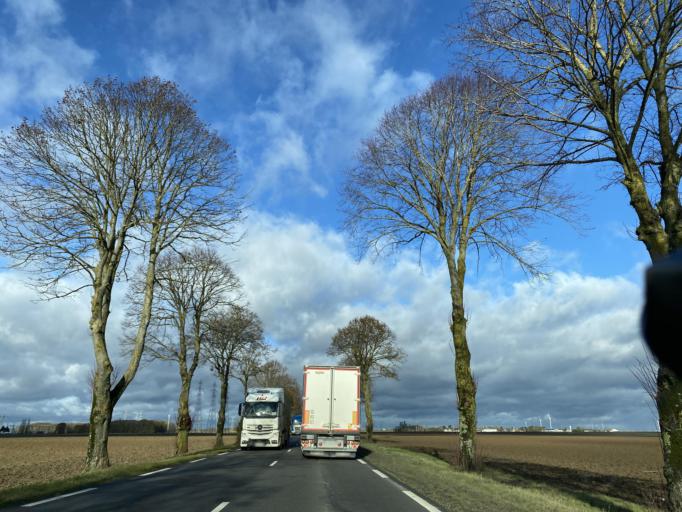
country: FR
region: Centre
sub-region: Departement du Loiret
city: Artenay
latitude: 48.0993
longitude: 1.8649
